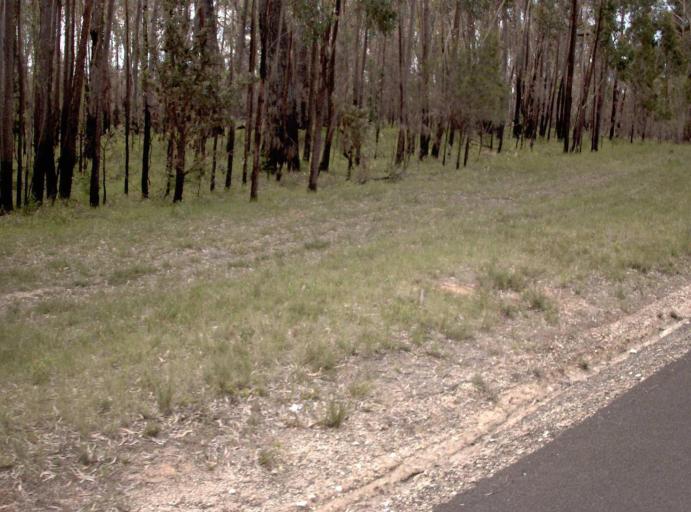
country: AU
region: New South Wales
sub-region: Bega Valley
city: Eden
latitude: -37.5120
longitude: 149.5127
